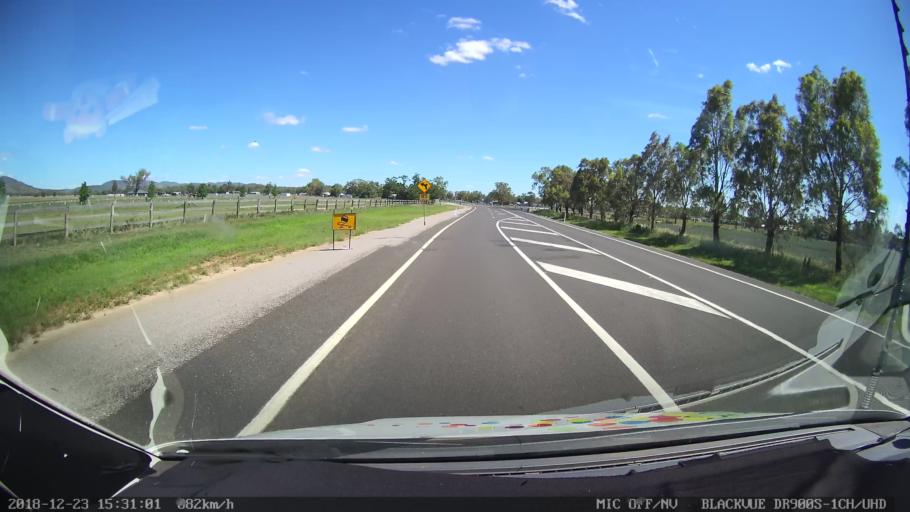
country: AU
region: New South Wales
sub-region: Tamworth Municipality
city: East Tamworth
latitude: -30.9663
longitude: 150.8663
